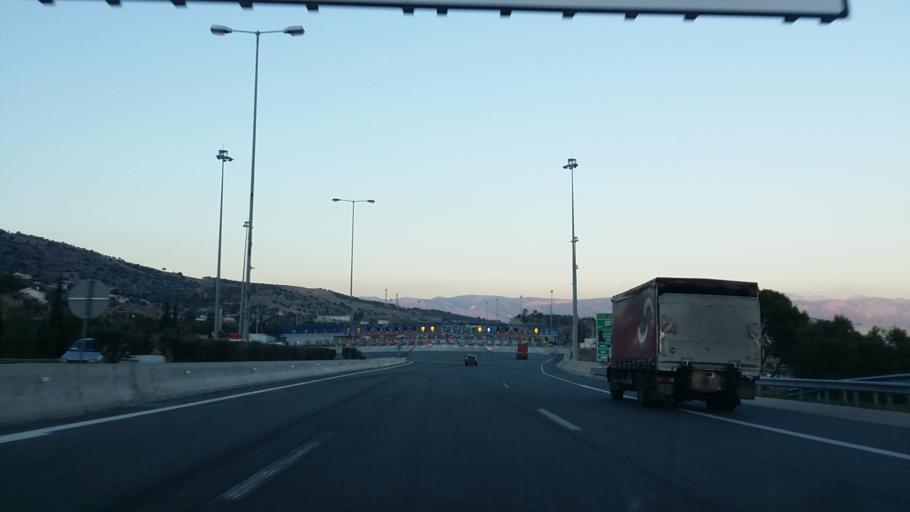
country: GR
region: Attica
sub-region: Nomarchia Dytikis Attikis
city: Mandra
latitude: 38.0385
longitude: 23.4932
